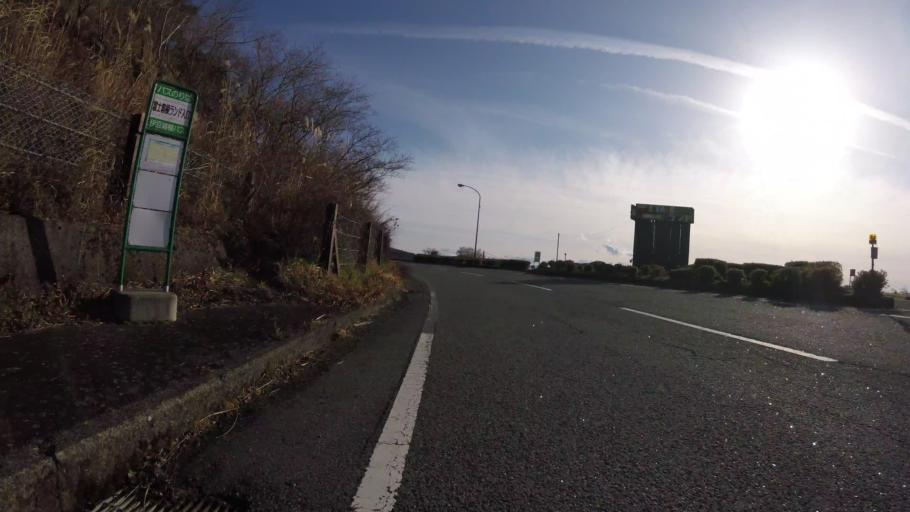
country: JP
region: Kanagawa
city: Hakone
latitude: 35.1711
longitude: 139.0208
